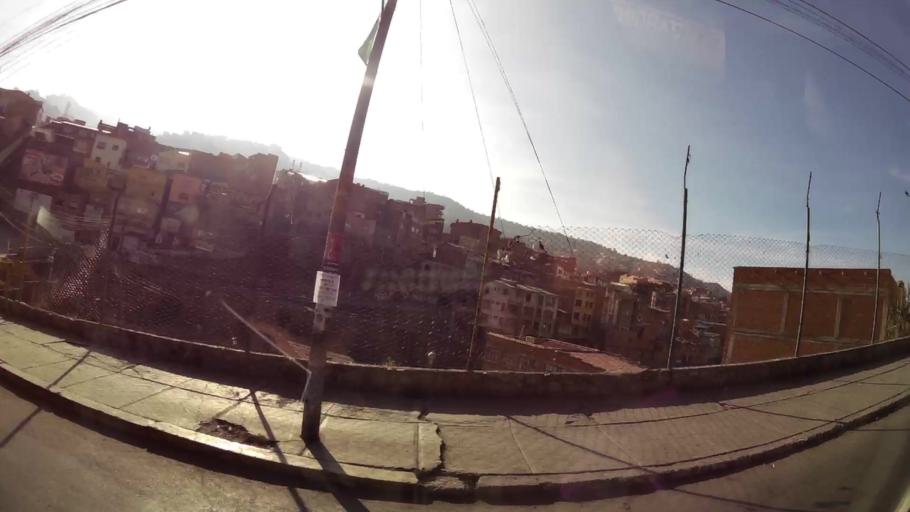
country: BO
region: La Paz
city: La Paz
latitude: -16.4966
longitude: -68.1184
